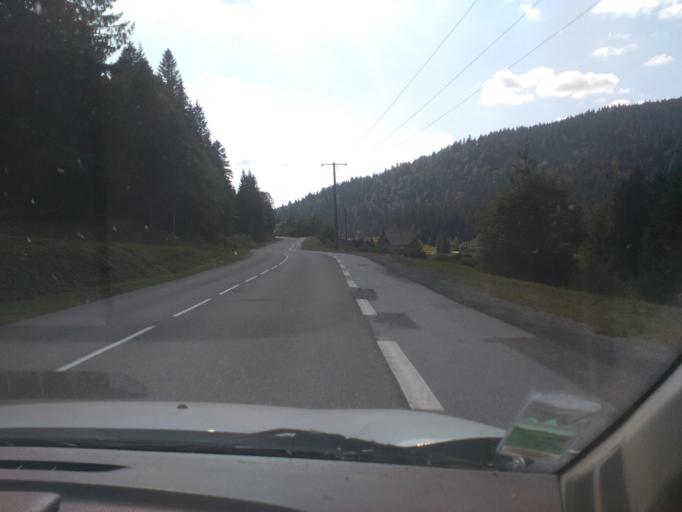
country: FR
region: Lorraine
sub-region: Departement des Vosges
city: Xonrupt-Longemer
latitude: 48.0497
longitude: 6.9396
